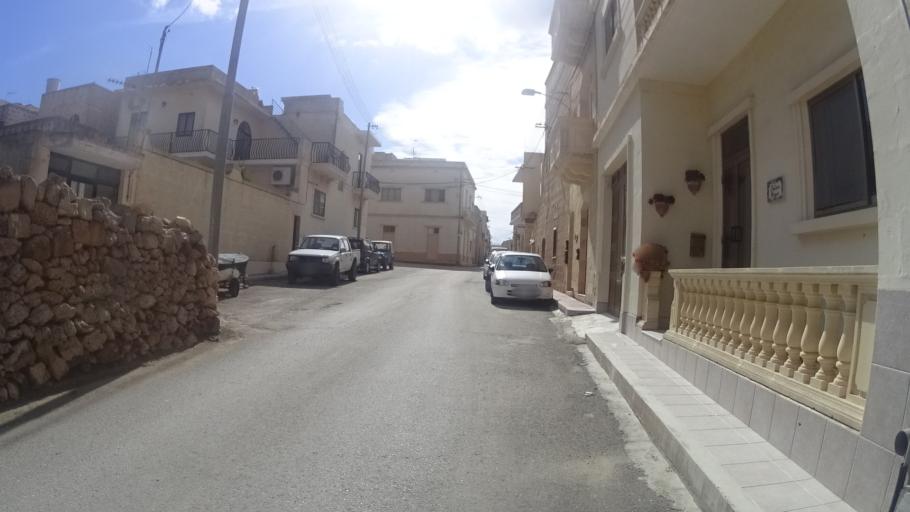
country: MT
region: In-Nadur
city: Nadur
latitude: 36.0504
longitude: 14.3002
